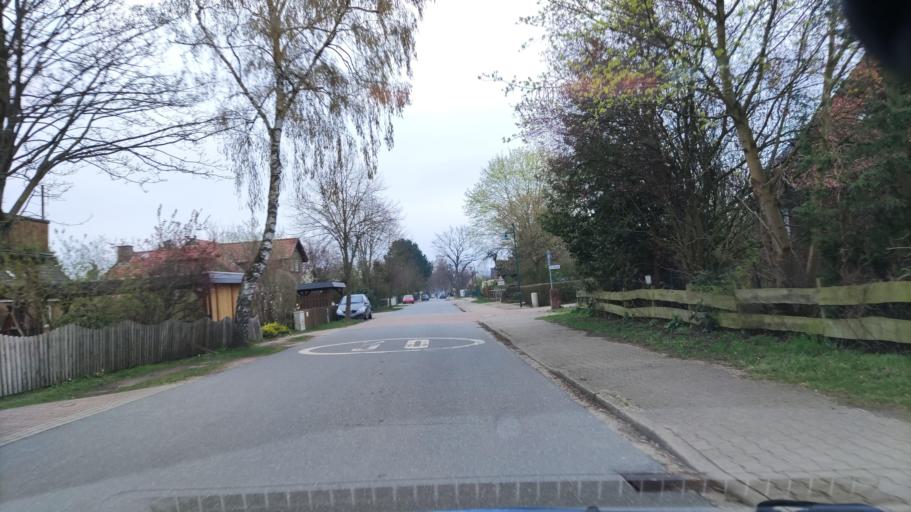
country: DE
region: Lower Saxony
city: Wulfsen
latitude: 53.3021
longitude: 10.1415
